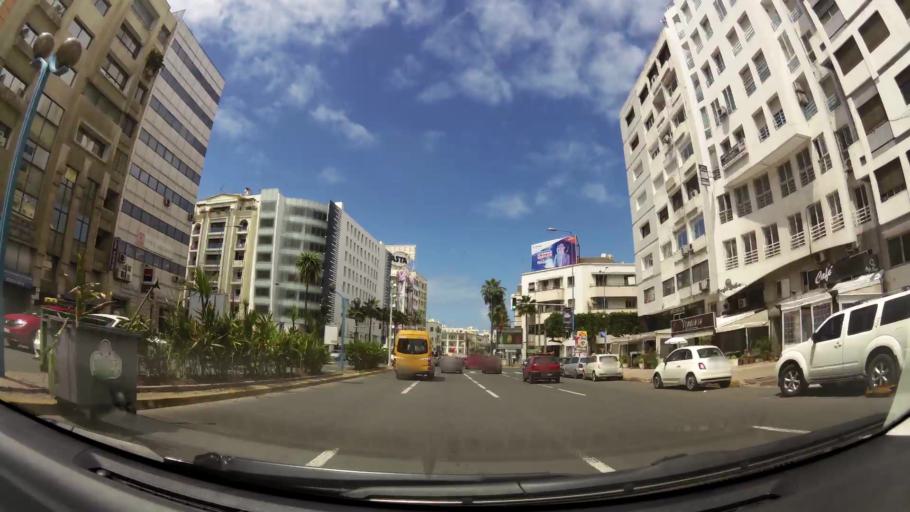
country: MA
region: Grand Casablanca
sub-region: Casablanca
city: Casablanca
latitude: 33.5924
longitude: -7.6369
